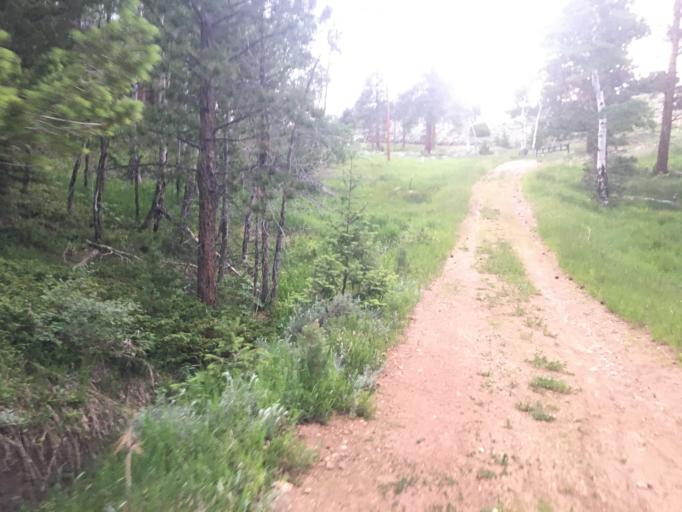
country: US
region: Colorado
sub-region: Larimer County
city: Estes Park
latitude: 40.3360
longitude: -105.5819
